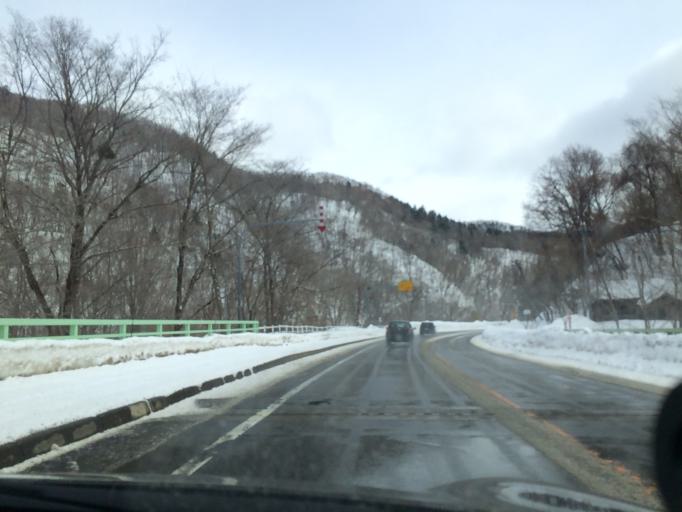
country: JP
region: Hokkaido
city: Iwamizawa
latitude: 43.0165
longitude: 141.9973
